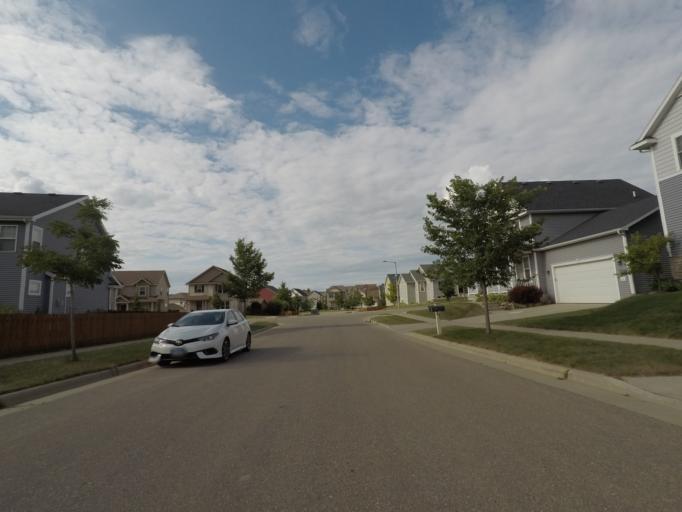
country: US
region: Wisconsin
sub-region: Dane County
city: Middleton
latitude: 43.0533
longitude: -89.5487
